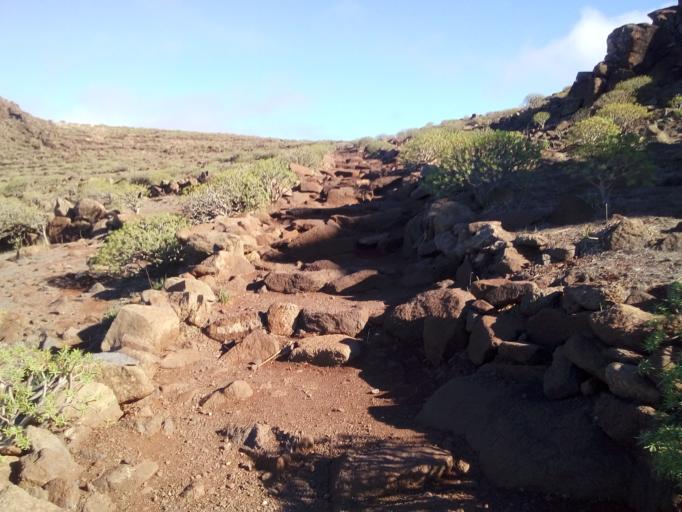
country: ES
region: Canary Islands
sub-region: Provincia de Santa Cruz de Tenerife
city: Vallehermosa
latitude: 28.1132
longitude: -17.3362
